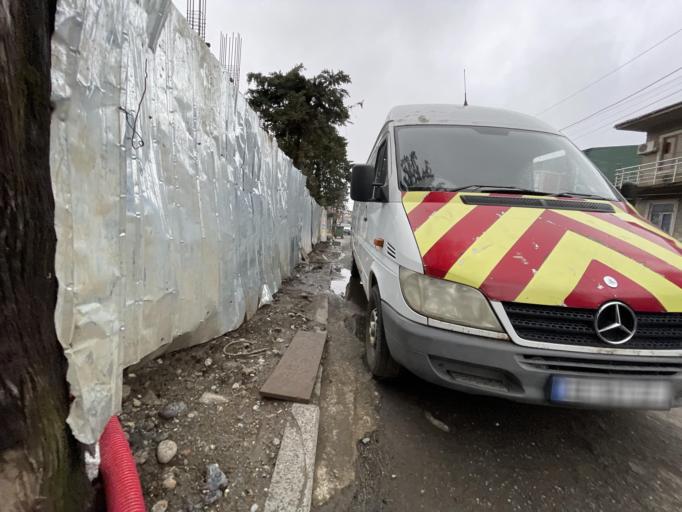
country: GE
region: Ajaria
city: Batumi
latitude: 41.6366
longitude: 41.6443
